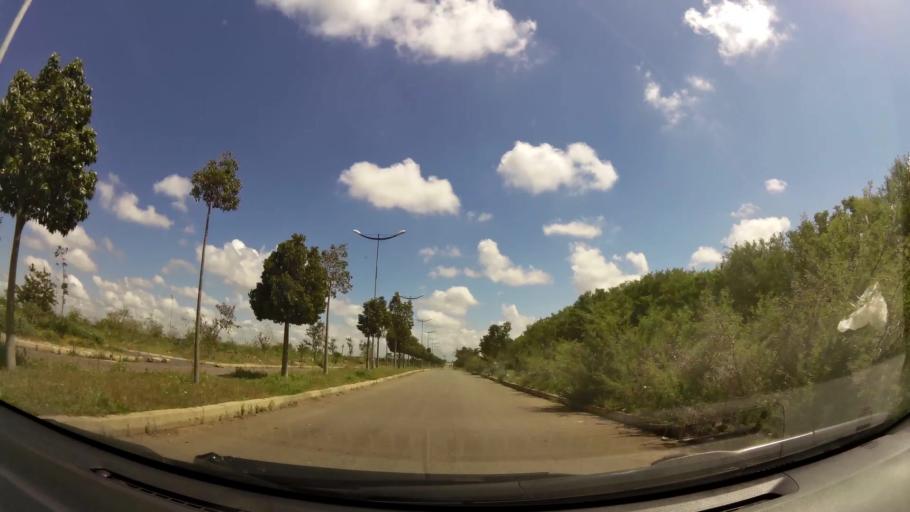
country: MA
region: Grand Casablanca
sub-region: Nouaceur
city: Dar Bouazza
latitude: 33.4163
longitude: -7.8324
